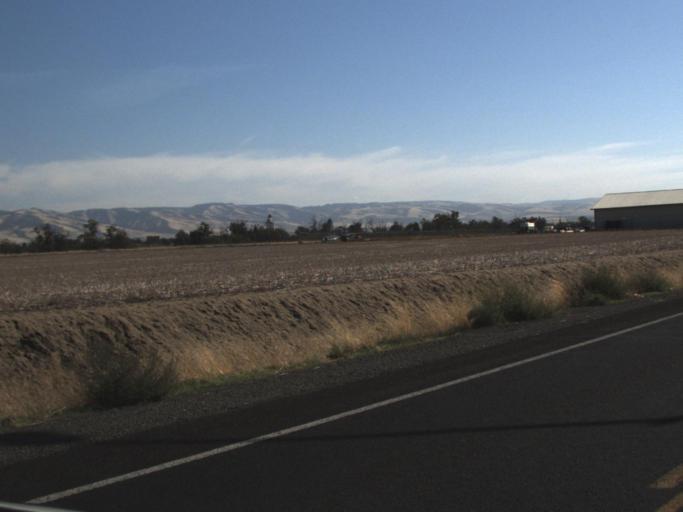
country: US
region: Washington
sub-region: Walla Walla County
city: Walla Walla
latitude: 46.0821
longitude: -118.3564
